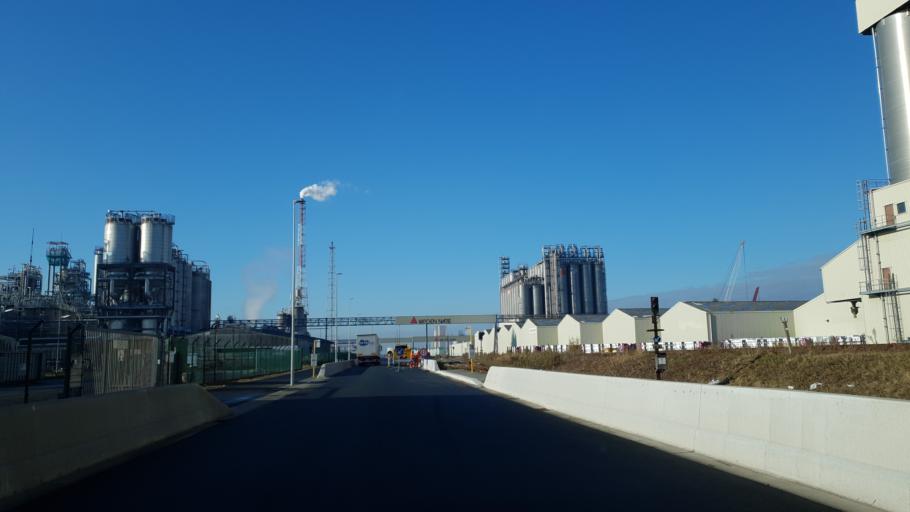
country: BE
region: Flanders
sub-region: Provincie Antwerpen
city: Antwerpen
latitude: 51.2439
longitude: 4.3767
